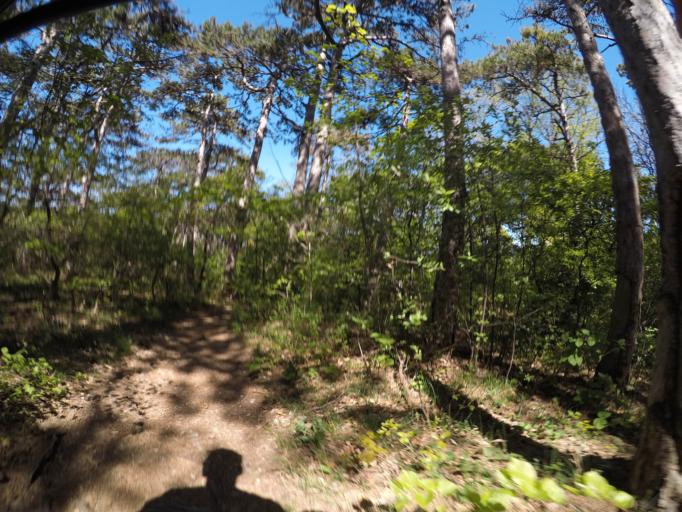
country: AT
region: Lower Austria
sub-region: Politischer Bezirk Modling
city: Modling
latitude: 48.0669
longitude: 16.2819
